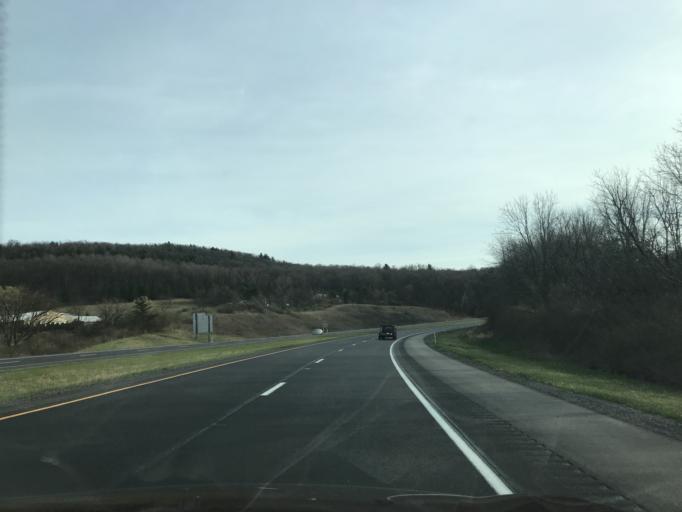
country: US
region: Pennsylvania
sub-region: Lycoming County
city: Muncy
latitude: 41.1933
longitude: -76.7700
